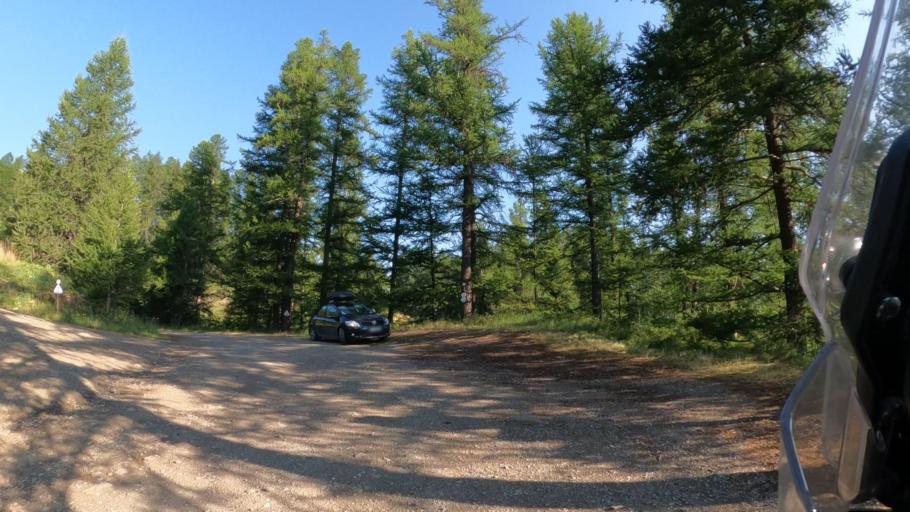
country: FR
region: Provence-Alpes-Cote d'Azur
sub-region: Departement des Hautes-Alpes
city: Guillestre
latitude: 44.6072
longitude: 6.6734
